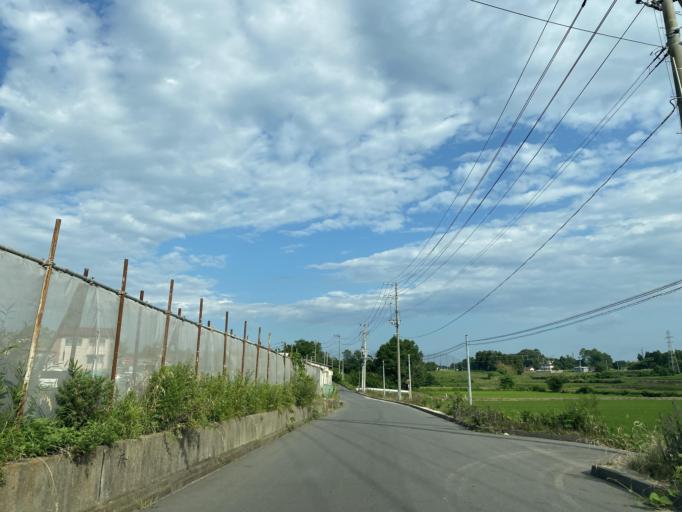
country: JP
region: Fukushima
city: Koriyama
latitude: 37.3496
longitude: 140.3419
